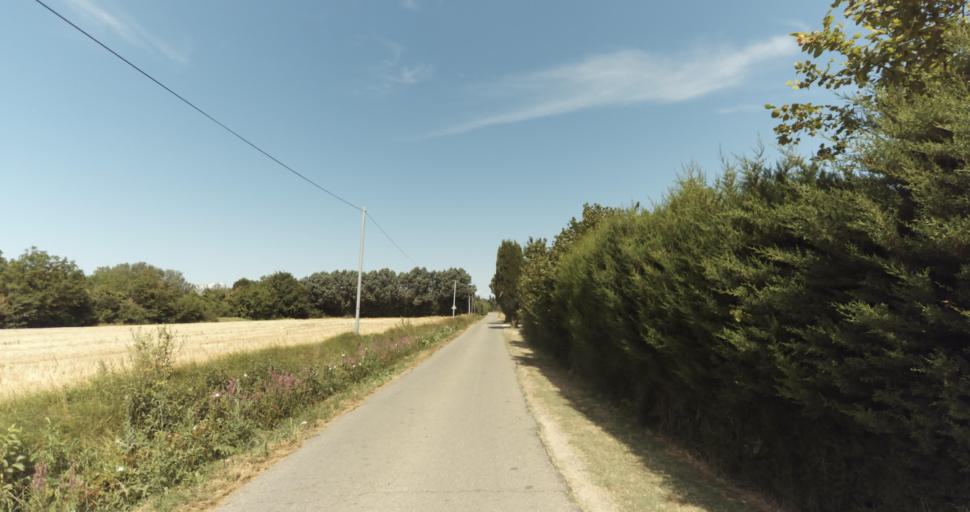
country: FR
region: Provence-Alpes-Cote d'Azur
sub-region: Departement du Vaucluse
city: Althen-des-Paluds
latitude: 44.0107
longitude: 4.9660
